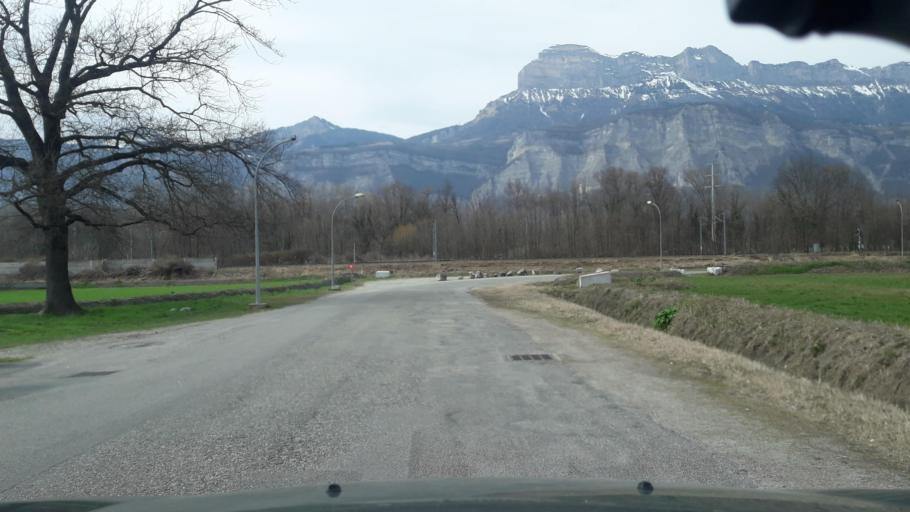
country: FR
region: Rhone-Alpes
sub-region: Departement de l'Isere
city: Froges
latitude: 45.2699
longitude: 5.9155
